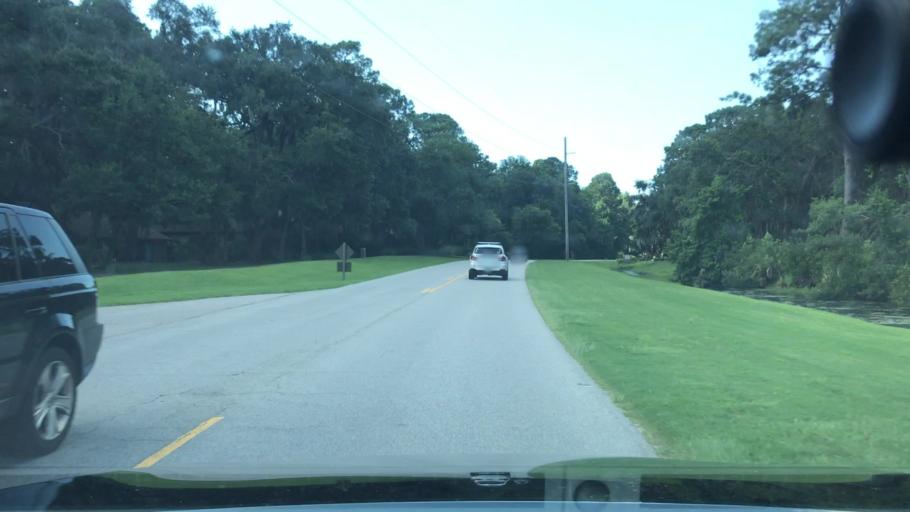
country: US
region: South Carolina
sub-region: Beaufort County
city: Hilton Head Island
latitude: 32.1400
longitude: -80.7878
